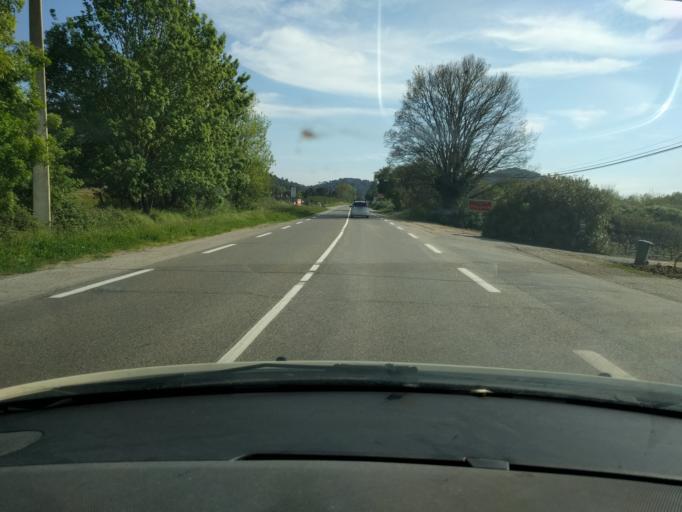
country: FR
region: Provence-Alpes-Cote d'Azur
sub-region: Departement du Var
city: La Crau
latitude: 43.1776
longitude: 6.1177
